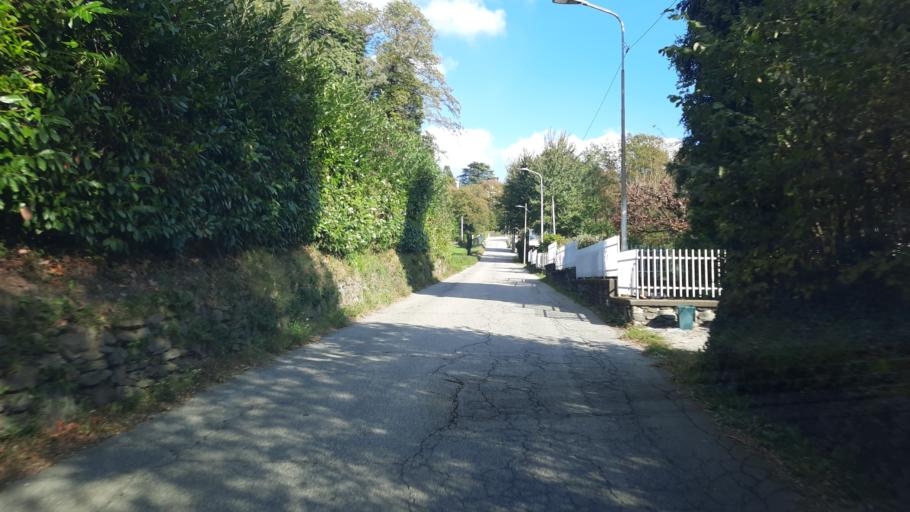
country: IT
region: Piedmont
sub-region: Provincia di Novara
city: Ameno
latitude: 45.7867
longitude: 8.4362
